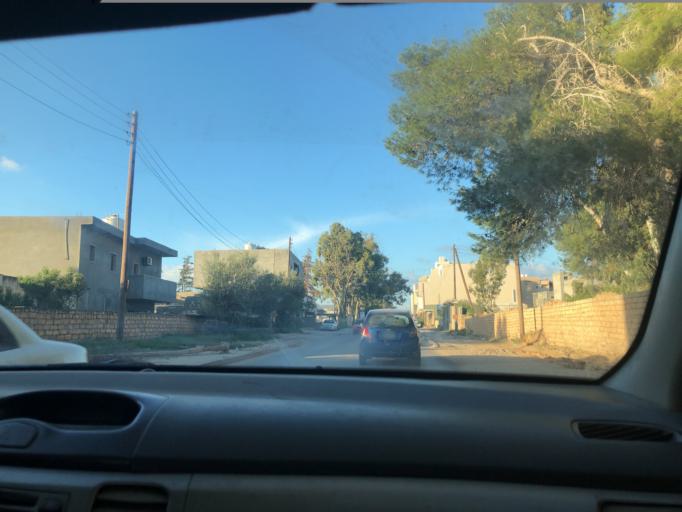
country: LY
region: Tripoli
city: Tagiura
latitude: 32.8561
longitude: 13.2790
